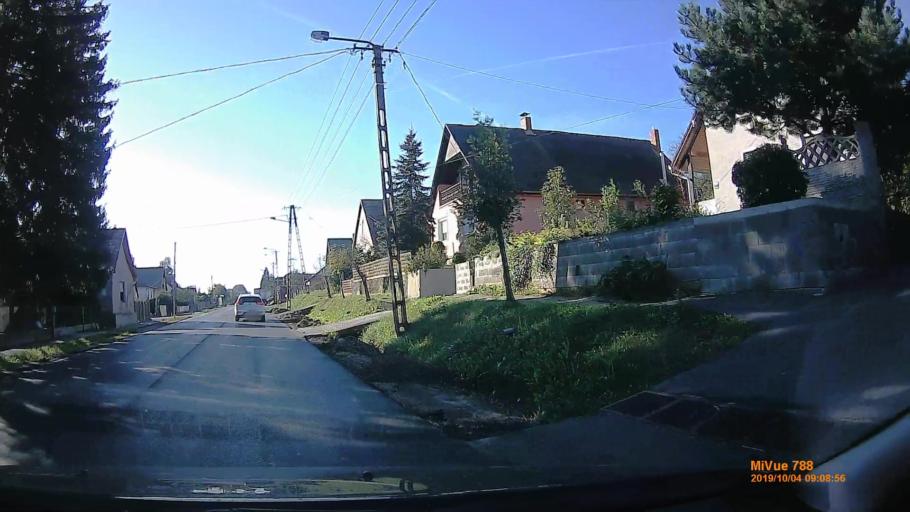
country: HU
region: Somogy
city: Karad
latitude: 46.6673
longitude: 17.7789
